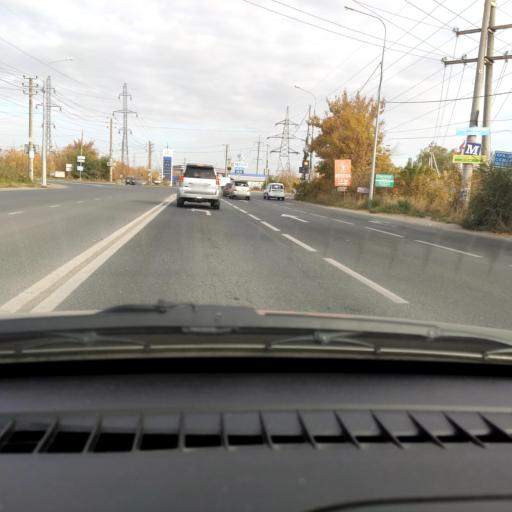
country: RU
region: Samara
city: Tol'yatti
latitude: 53.5776
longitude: 49.2936
